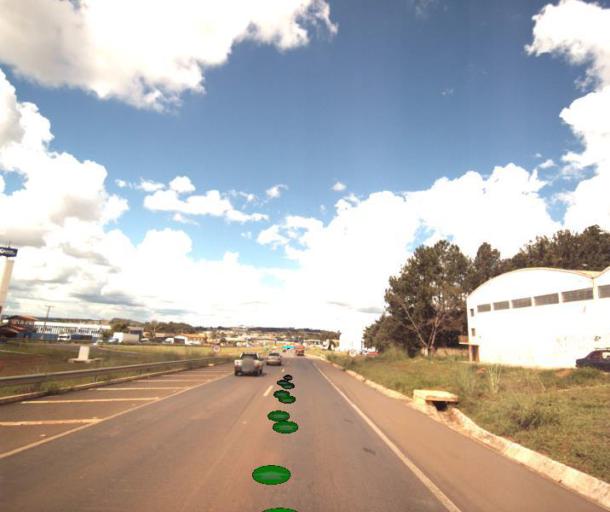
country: BR
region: Goias
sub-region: Anapolis
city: Anapolis
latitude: -16.3534
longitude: -48.9205
